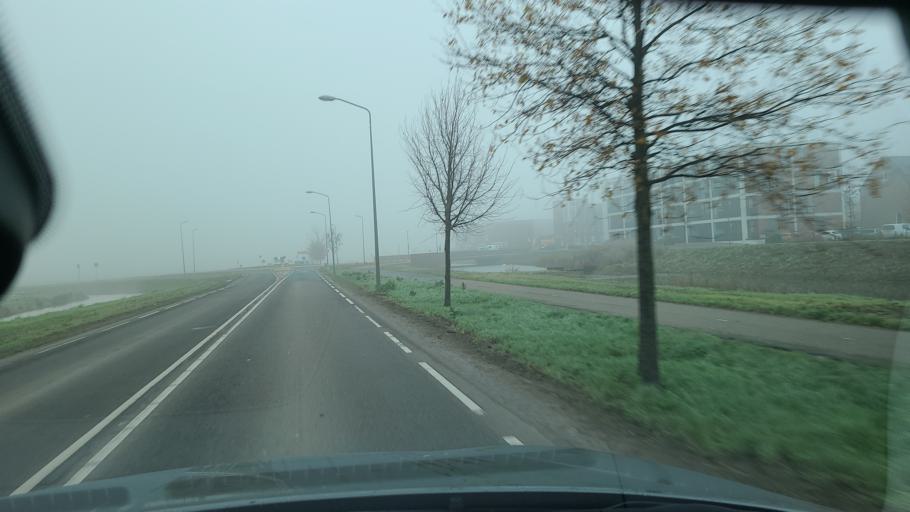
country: NL
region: North Brabant
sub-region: Gemeente 's-Hertogenbosch
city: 's-Hertogenbosch
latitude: 51.7340
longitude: 5.3458
